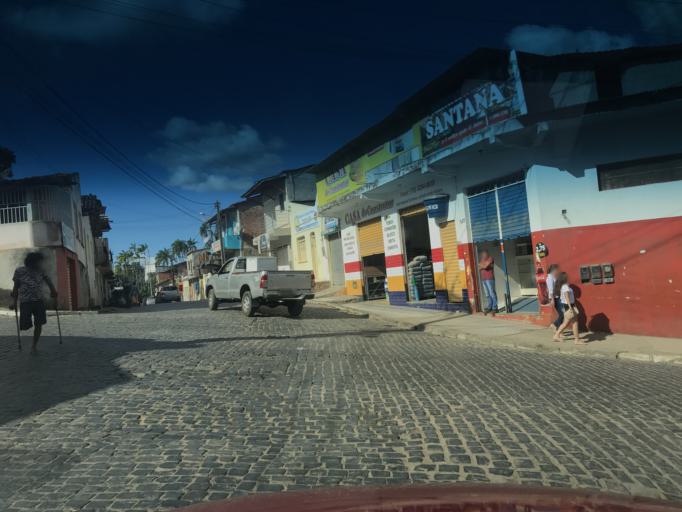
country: BR
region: Bahia
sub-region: Gandu
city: Gandu
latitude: -13.7469
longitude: -39.4898
